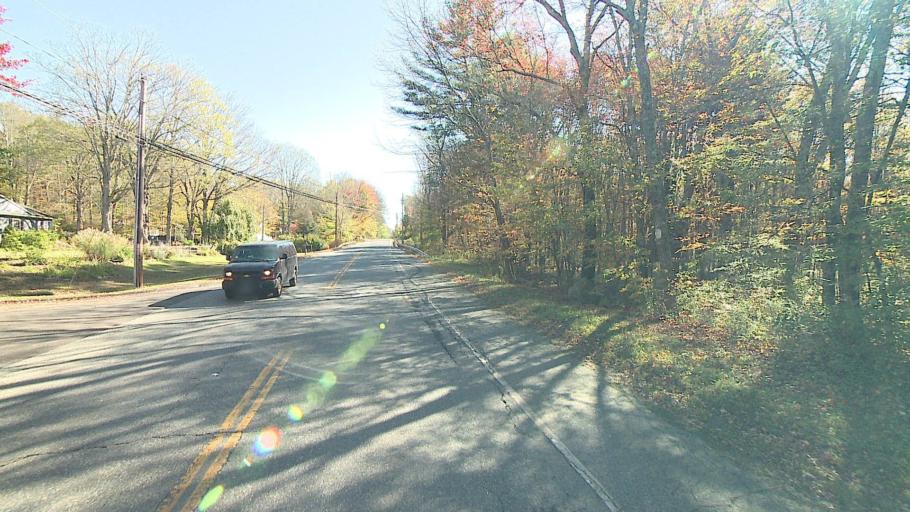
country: US
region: Connecticut
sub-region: Hartford County
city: Terramuggus
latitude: 41.6482
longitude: -72.4227
